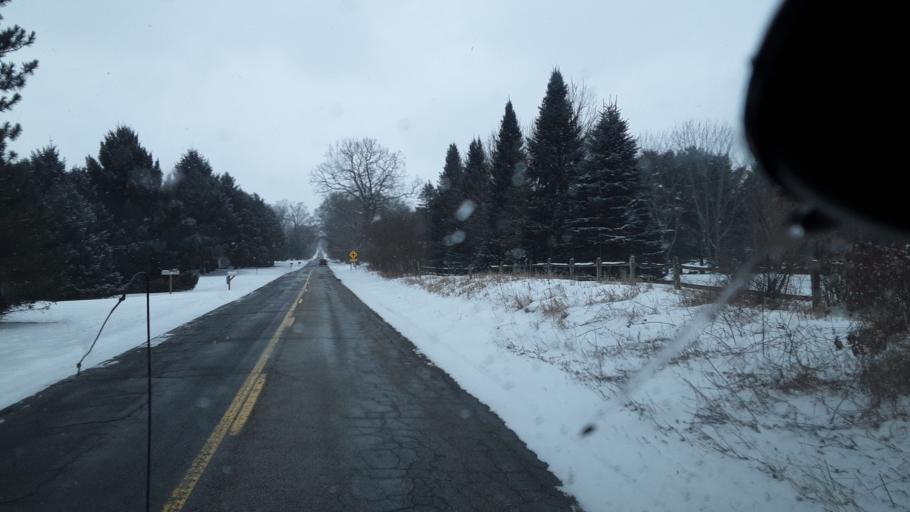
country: US
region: Michigan
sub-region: Ingham County
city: Leslie
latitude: 42.4826
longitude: -84.3942
